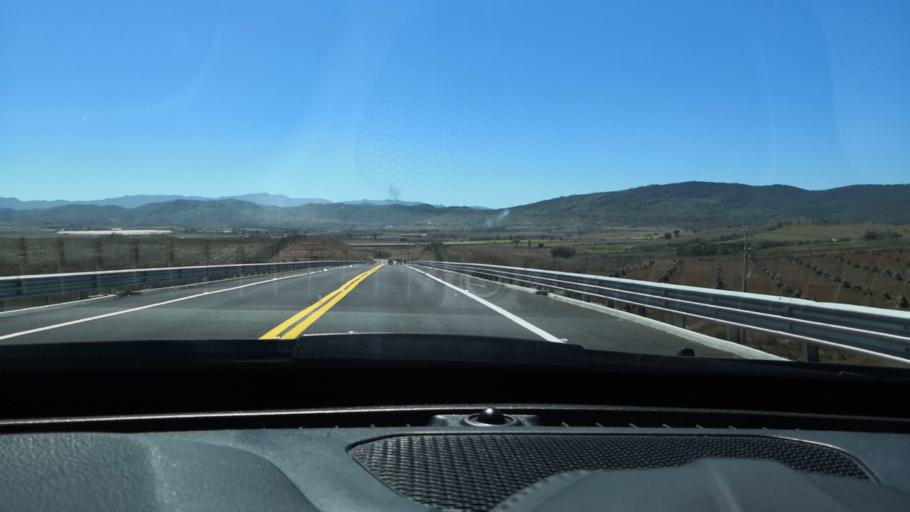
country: MX
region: Nayarit
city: Compostela
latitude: 21.2174
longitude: -104.8815
